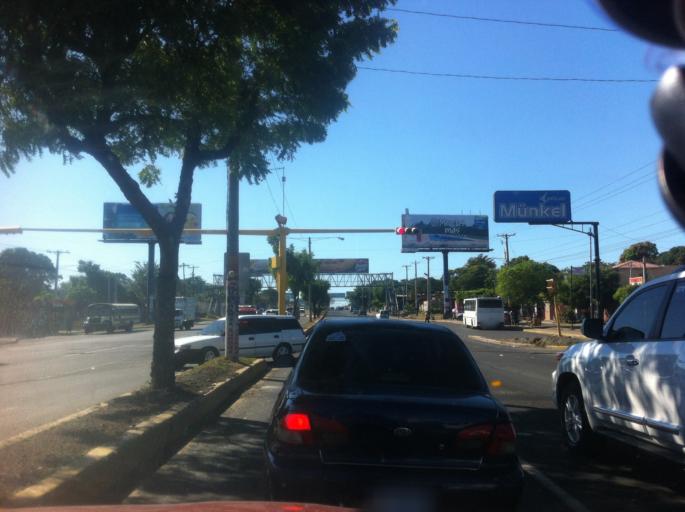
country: NI
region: Managua
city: Managua
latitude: 12.1474
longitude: -86.1885
